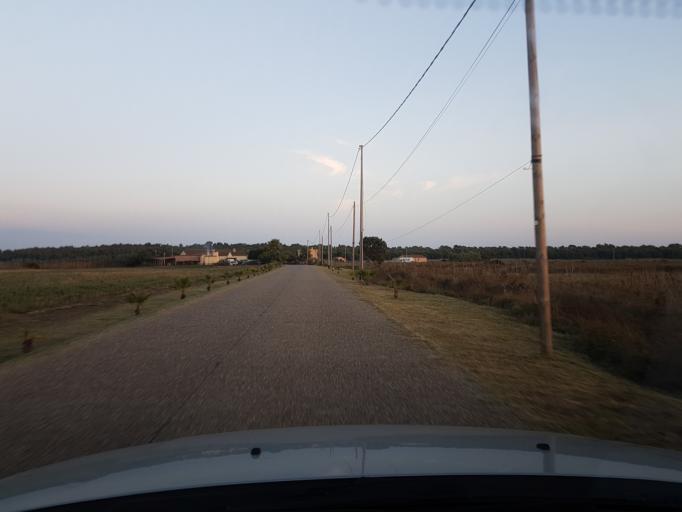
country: IT
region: Sardinia
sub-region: Provincia di Oristano
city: Cabras
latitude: 39.9157
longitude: 8.5084
